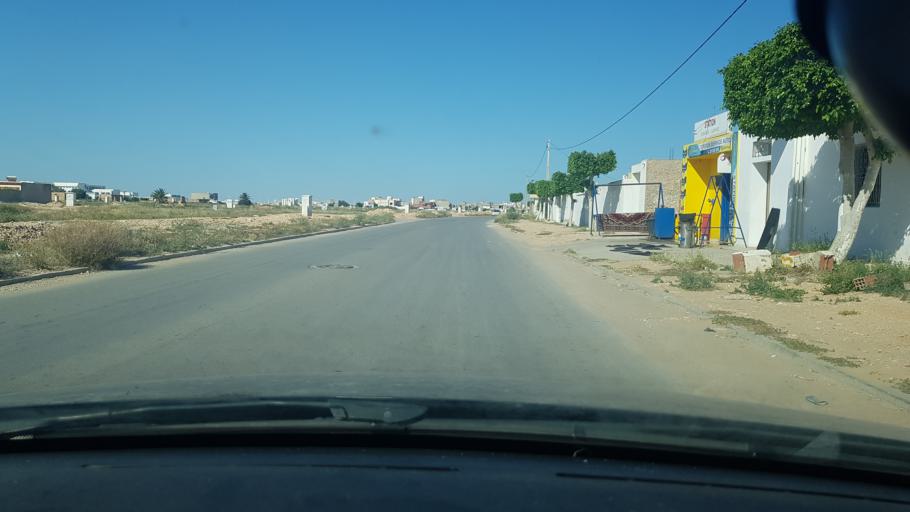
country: TN
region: Safaqis
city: Al Qarmadah
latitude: 34.8213
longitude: 10.7417
